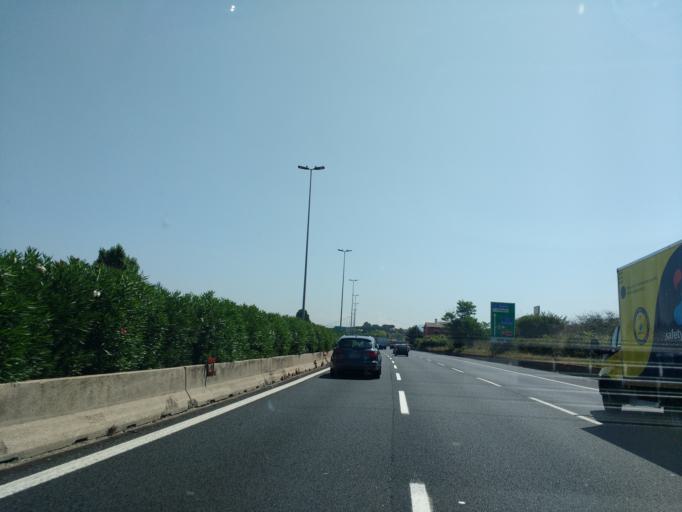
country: IT
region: Latium
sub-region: Citta metropolitana di Roma Capitale
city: Borgo Lotti
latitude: 41.7951
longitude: 12.5240
